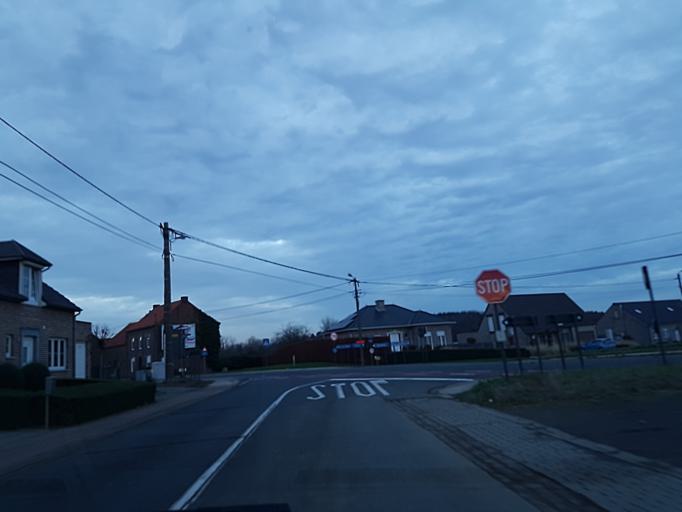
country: BE
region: Flanders
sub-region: Provincie Vlaams-Brabant
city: Lubbeek
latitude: 50.8649
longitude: 4.8903
